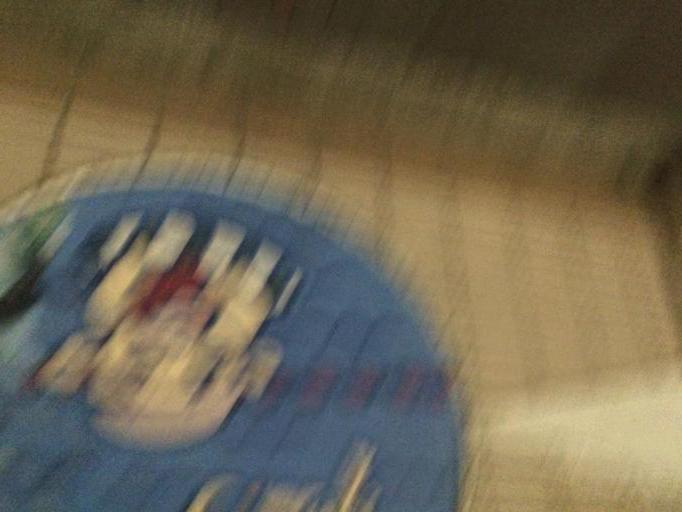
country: TW
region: Taipei
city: Taipei
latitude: 25.0258
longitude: 121.5035
